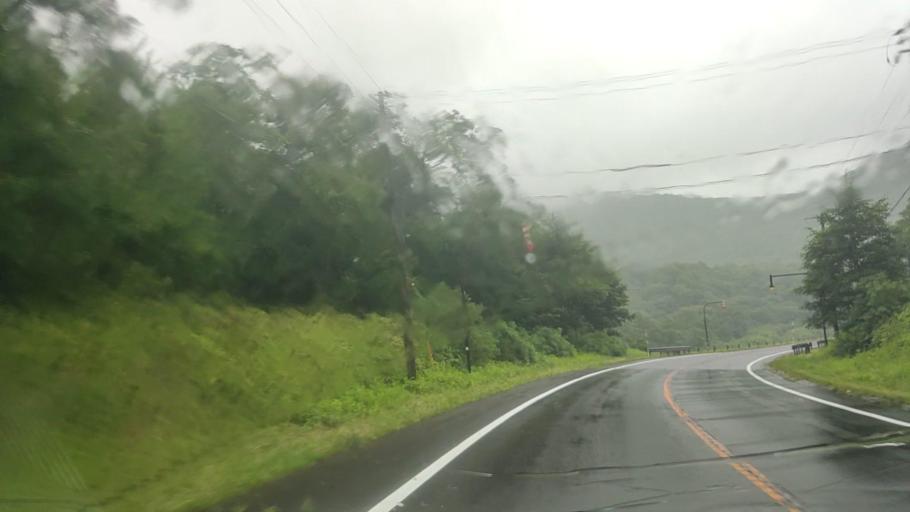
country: JP
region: Hokkaido
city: Muroran
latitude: 42.5136
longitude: 141.1145
